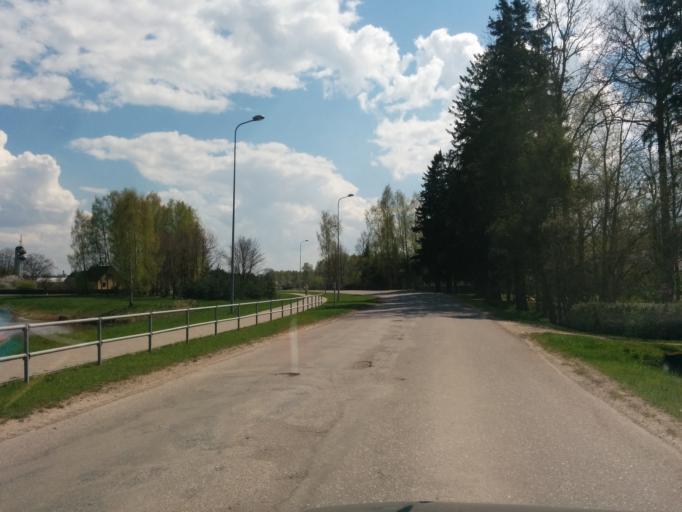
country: LV
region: Jelgava
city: Jelgava
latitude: 56.6196
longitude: 23.7720
